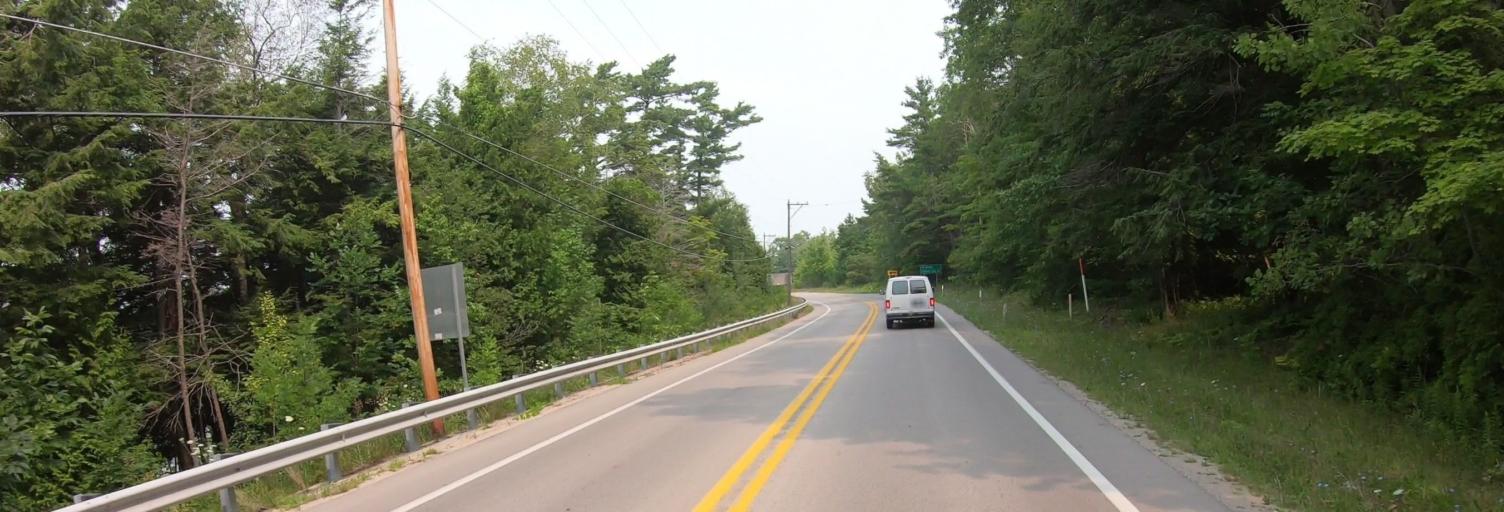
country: US
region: Michigan
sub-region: Leelanau County
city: Leland
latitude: 44.9931
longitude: -85.7696
